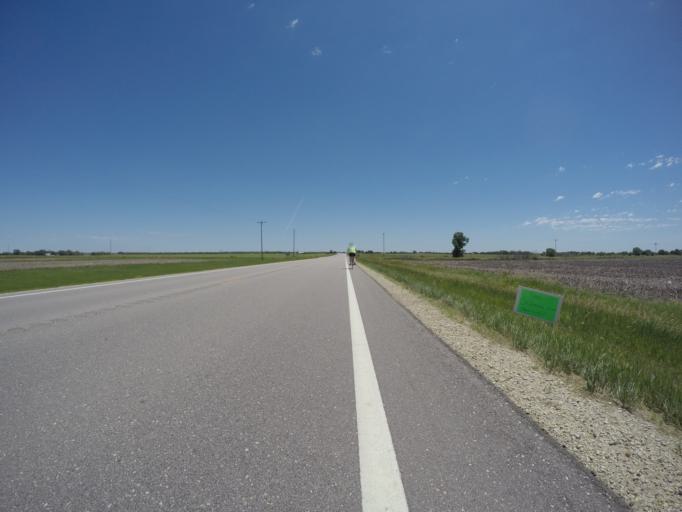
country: US
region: Kansas
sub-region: Republic County
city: Belleville
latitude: 39.8127
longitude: -97.6722
